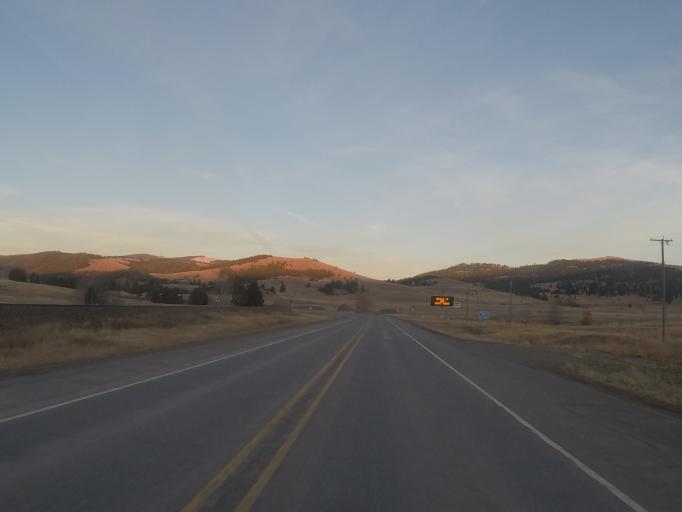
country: US
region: Montana
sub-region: Lewis and Clark County
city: Helena West Side
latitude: 46.5567
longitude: -112.3997
